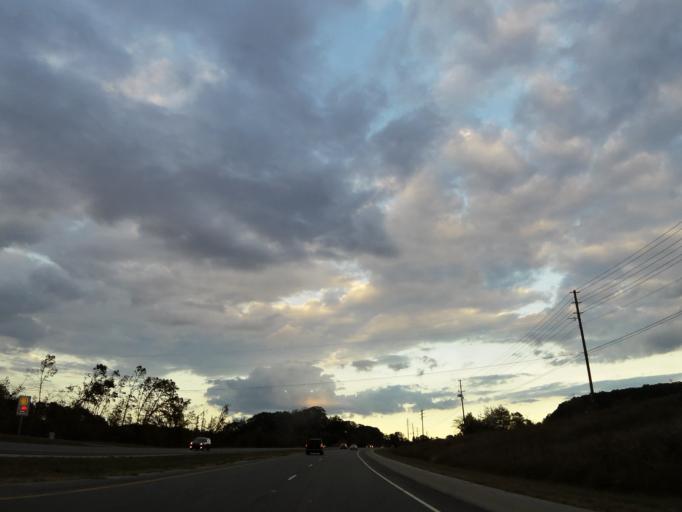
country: US
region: Tennessee
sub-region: Blount County
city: Louisville
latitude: 35.7559
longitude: -84.0926
